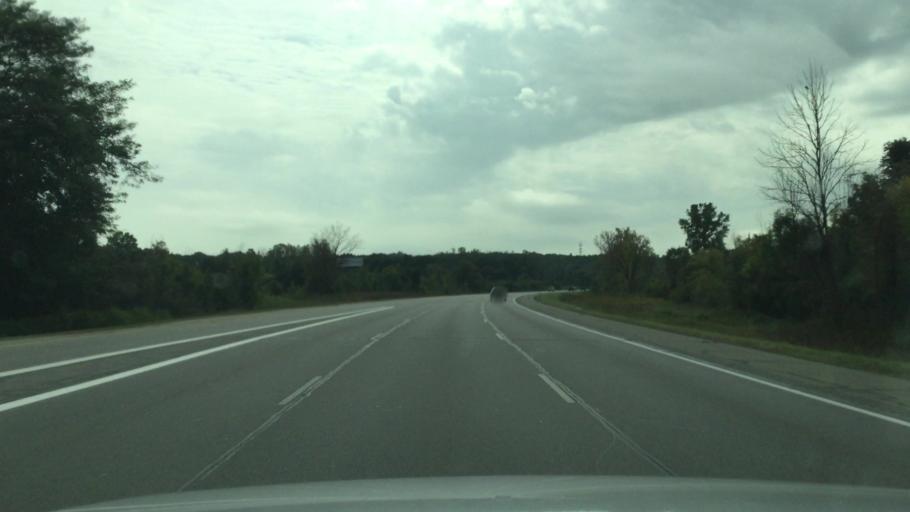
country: US
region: Michigan
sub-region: Genesee County
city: Grand Blanc
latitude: 42.8694
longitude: -83.5944
